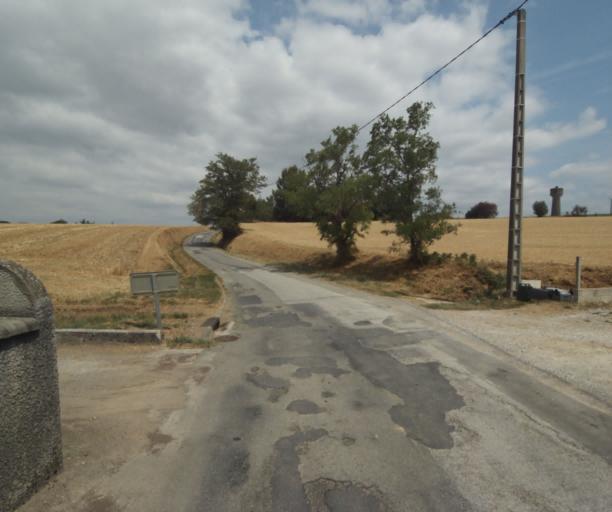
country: FR
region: Midi-Pyrenees
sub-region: Departement de la Haute-Garonne
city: Revel
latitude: 43.4367
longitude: 1.9689
